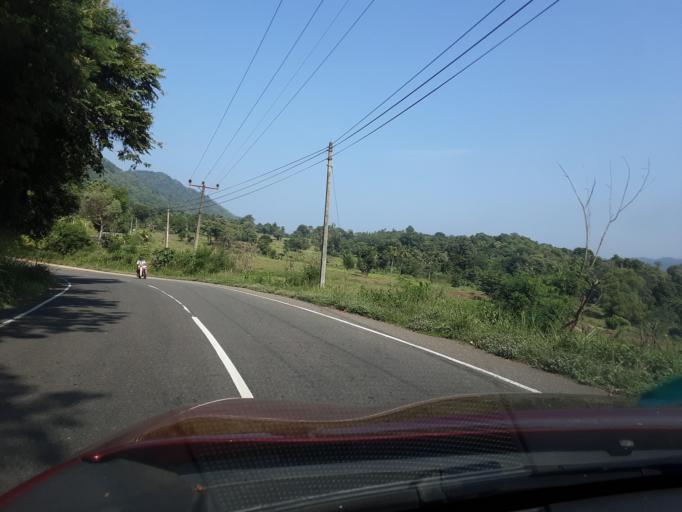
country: LK
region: Uva
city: Badulla
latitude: 7.1520
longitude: 81.0580
